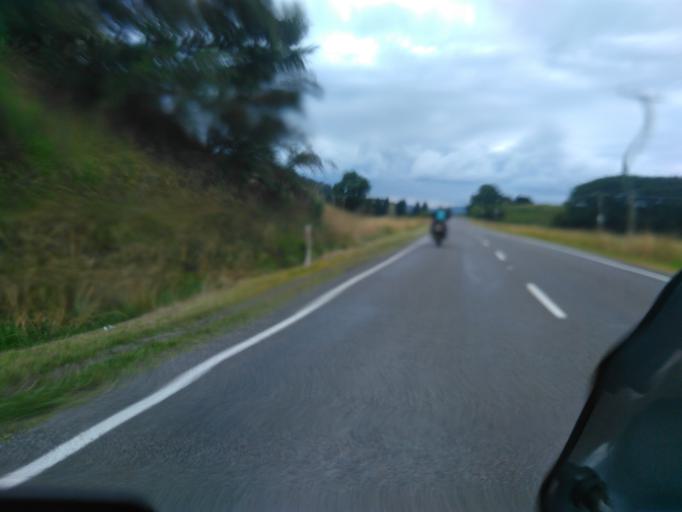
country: NZ
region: Gisborne
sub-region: Gisborne District
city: Gisborne
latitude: -38.4548
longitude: 177.7754
